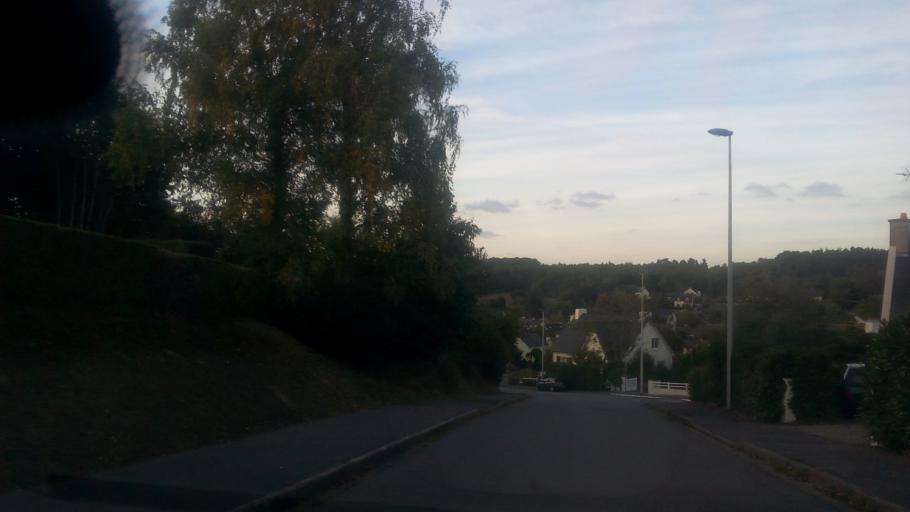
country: FR
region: Brittany
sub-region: Departement d'Ille-et-Vilaine
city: Redon
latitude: 47.6589
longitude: -2.0895
